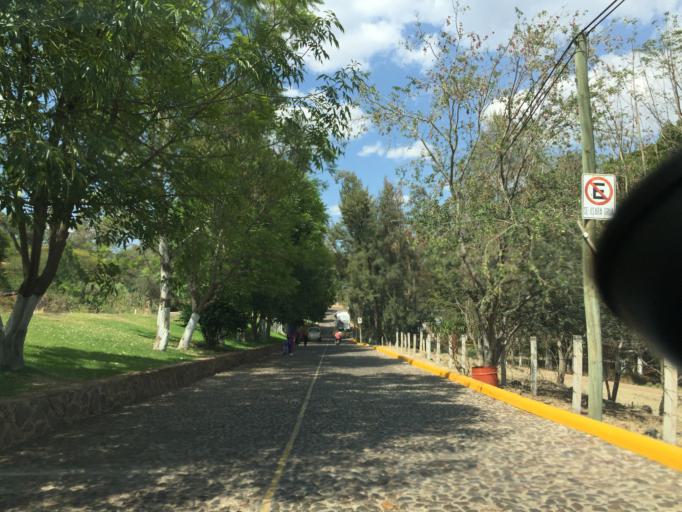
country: MX
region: Jalisco
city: Atotonilco el Alto
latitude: 20.5640
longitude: -102.4797
